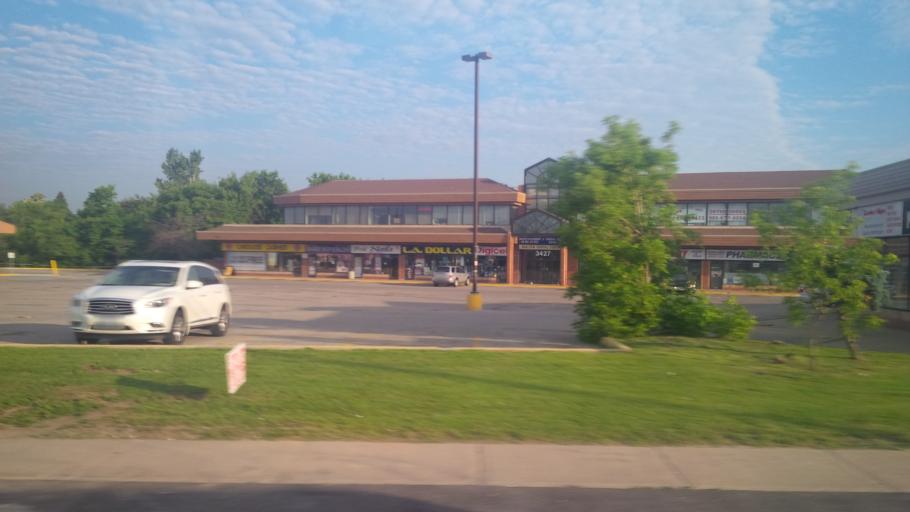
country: CA
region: Ontario
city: Etobicoke
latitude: 43.7132
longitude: -79.6324
